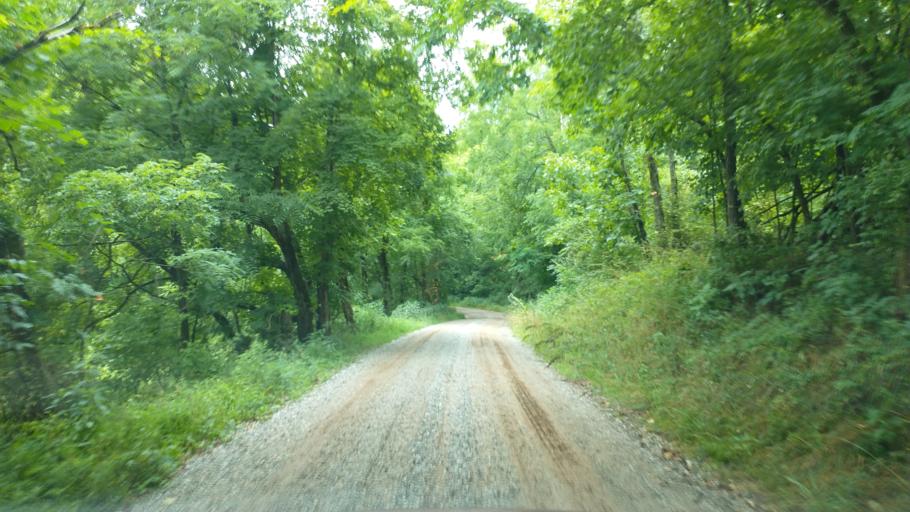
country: US
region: Ohio
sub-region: Meigs County
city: Middleport
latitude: 38.9242
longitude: -82.0457
